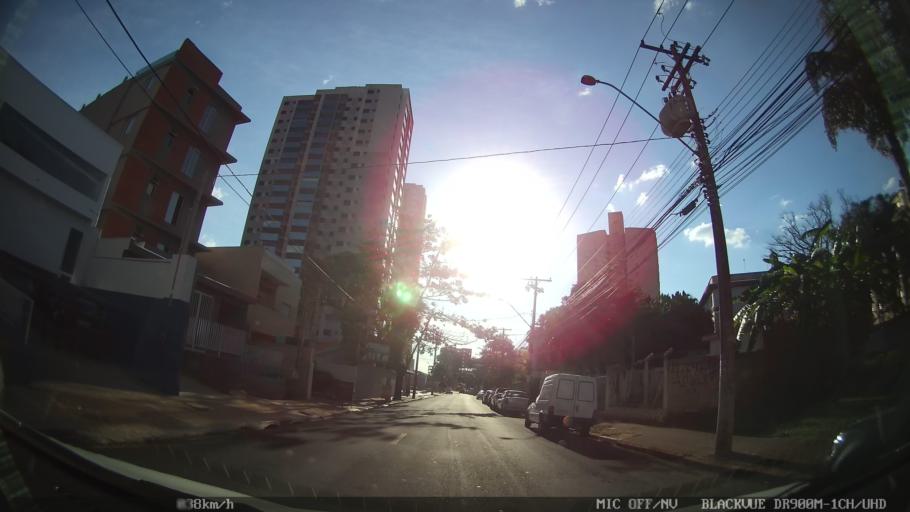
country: BR
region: Sao Paulo
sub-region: Ribeirao Preto
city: Ribeirao Preto
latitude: -21.1926
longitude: -47.7848
